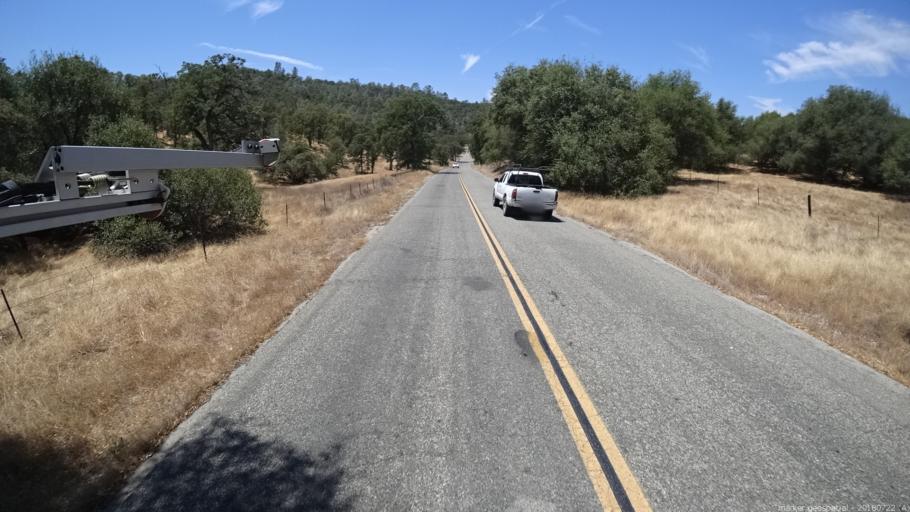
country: US
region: California
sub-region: Madera County
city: Coarsegold
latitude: 37.2500
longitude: -119.7290
